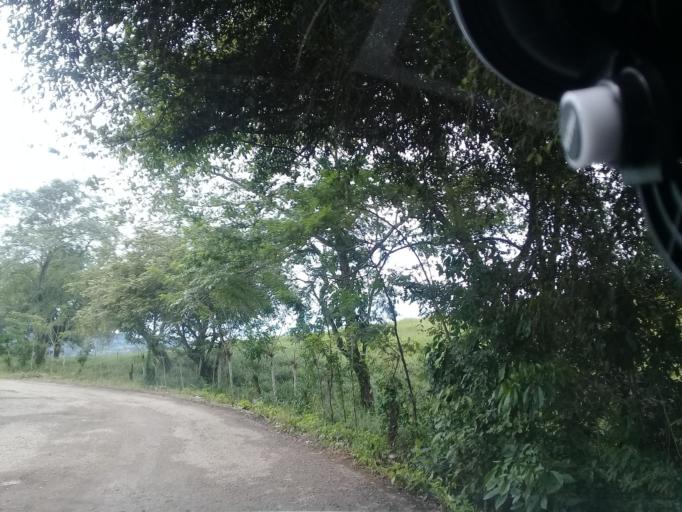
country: MX
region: Veracruz
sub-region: Chalma
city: San Pedro Coyutla
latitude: 21.2126
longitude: -98.3840
